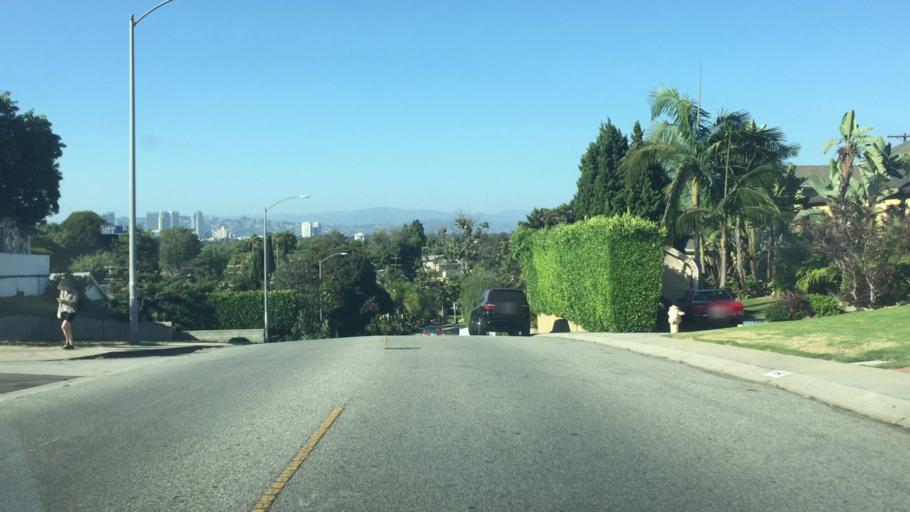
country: US
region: California
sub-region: Los Angeles County
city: Culver City
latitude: 34.0138
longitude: -118.4332
